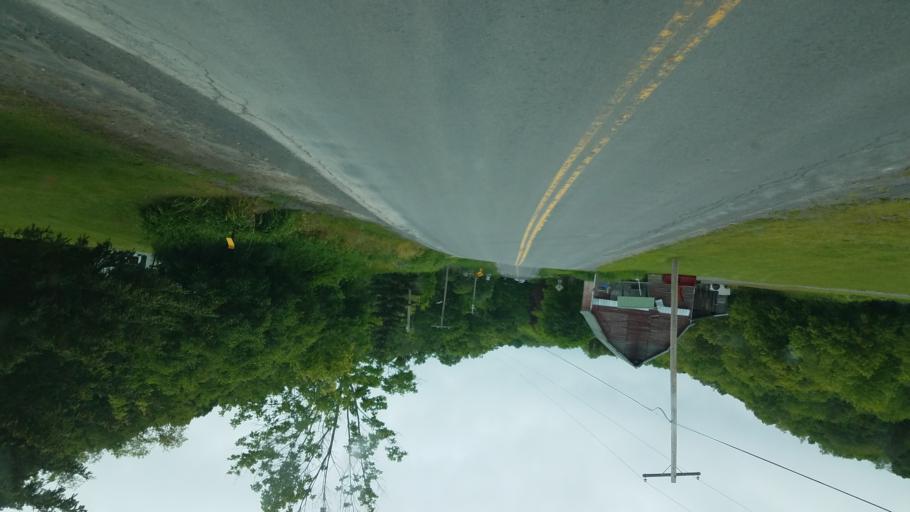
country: US
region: New York
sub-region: Oneida County
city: Chadwicks
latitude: 42.9772
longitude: -75.2348
